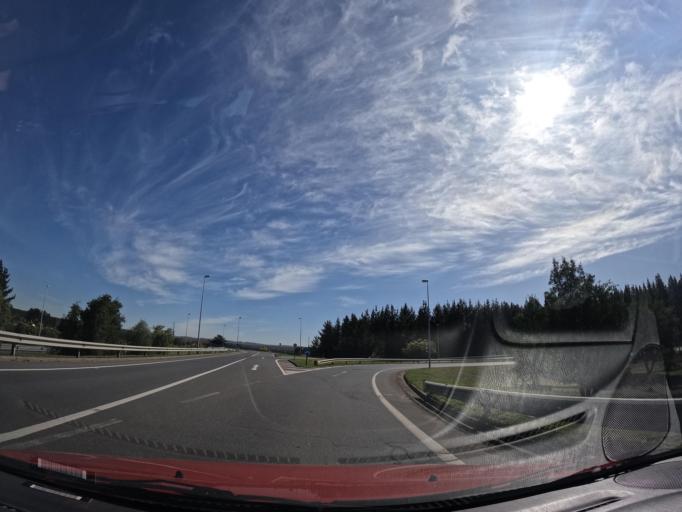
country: CL
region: Biobio
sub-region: Provincia de Biobio
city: Cabrero
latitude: -36.9328
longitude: -72.3493
